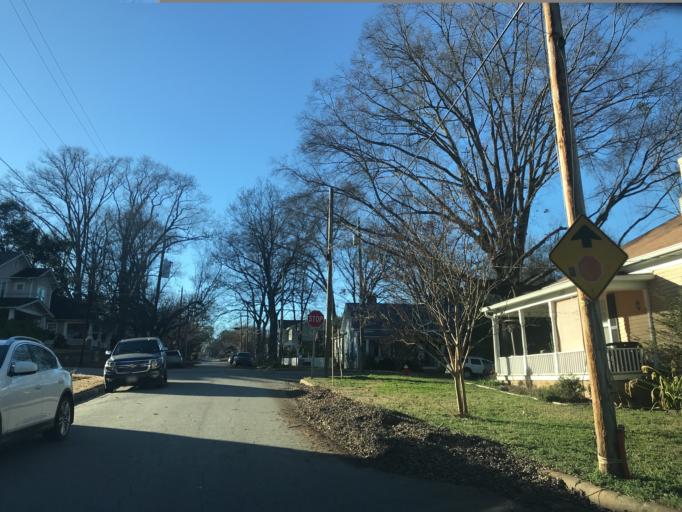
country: US
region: North Carolina
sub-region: Wake County
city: West Raleigh
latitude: 35.7952
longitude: -78.6446
